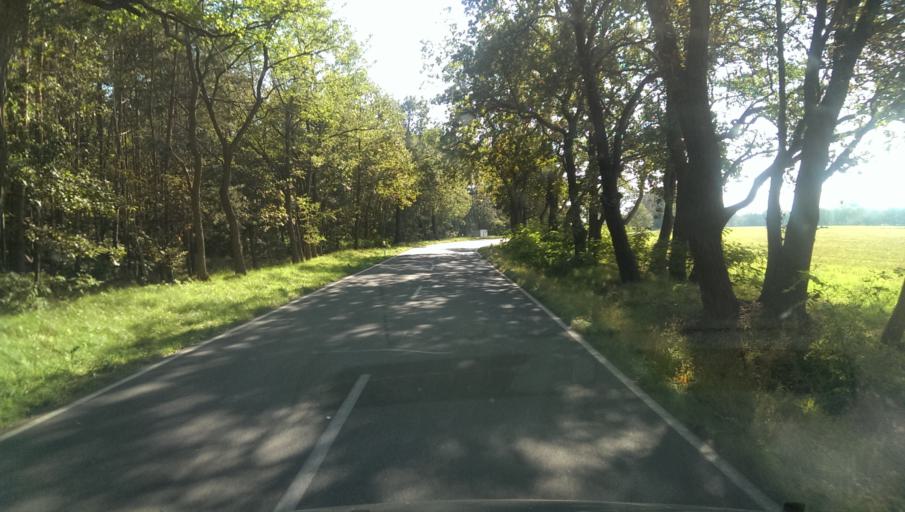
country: DE
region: Brandenburg
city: Halbe
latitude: 52.0838
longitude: 13.7309
